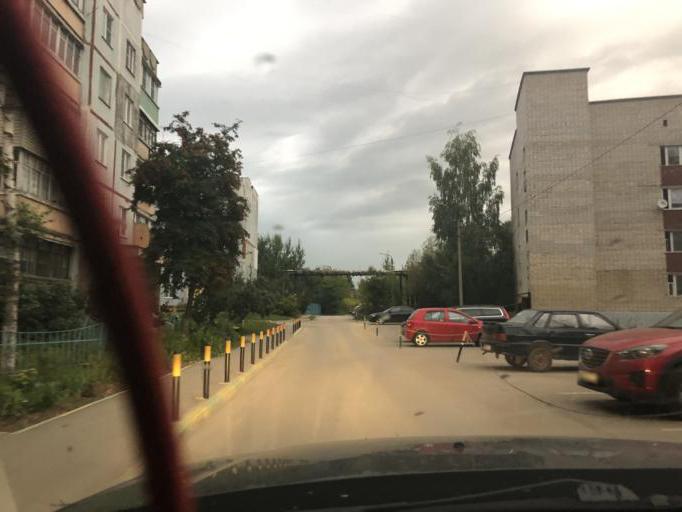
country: RU
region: Tula
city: Gorelki
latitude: 54.2277
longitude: 37.6150
